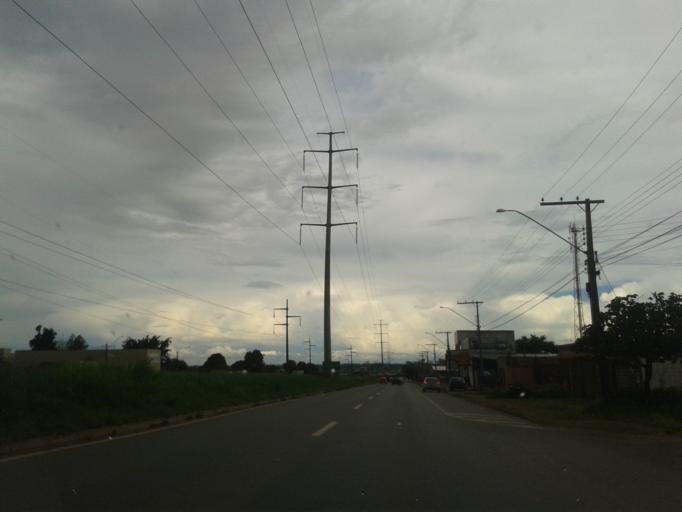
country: BR
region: Goias
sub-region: Aparecida De Goiania
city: Aparecida de Goiania
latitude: -16.7835
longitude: -49.2744
